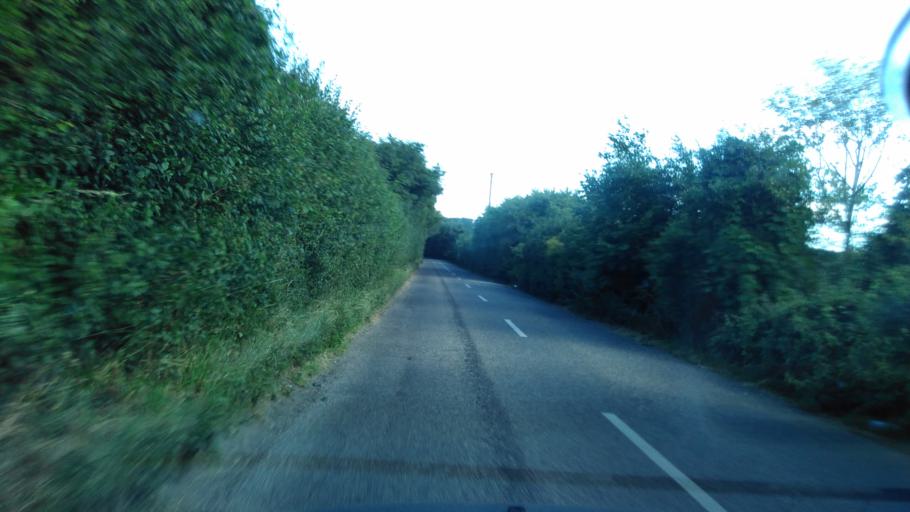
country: GB
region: England
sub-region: Kent
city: Dunkirk
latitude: 51.2544
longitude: 0.9572
